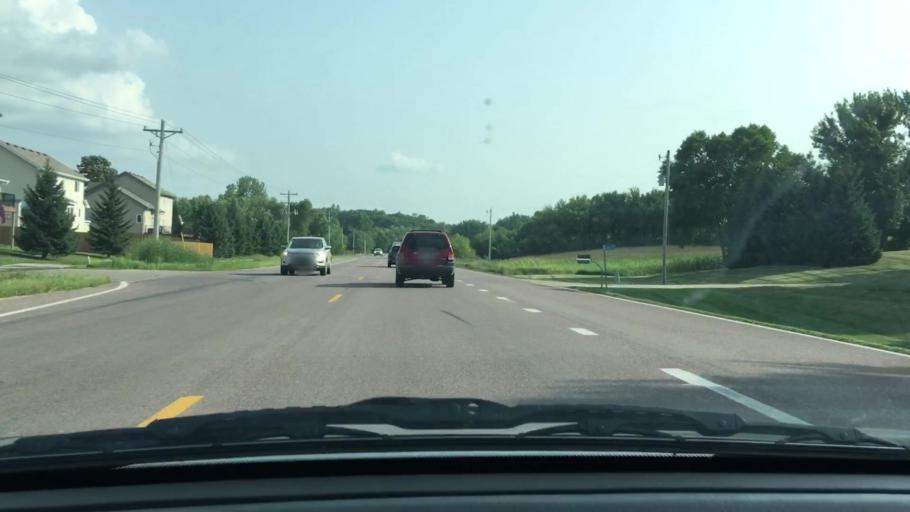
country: US
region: Minnesota
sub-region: Scott County
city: Elko New Market
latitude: 44.5637
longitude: -93.3388
